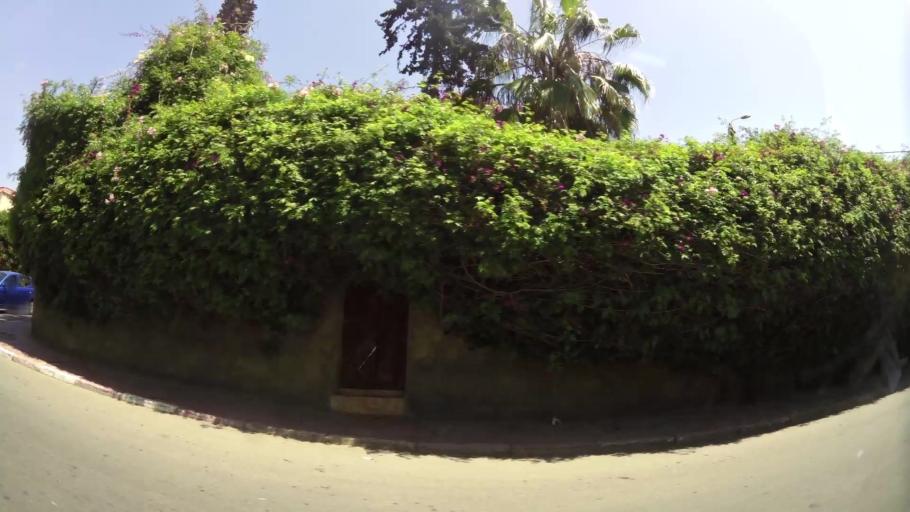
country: MA
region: Souss-Massa-Draa
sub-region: Agadir-Ida-ou-Tnan
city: Agadir
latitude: 30.4312
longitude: -9.5903
